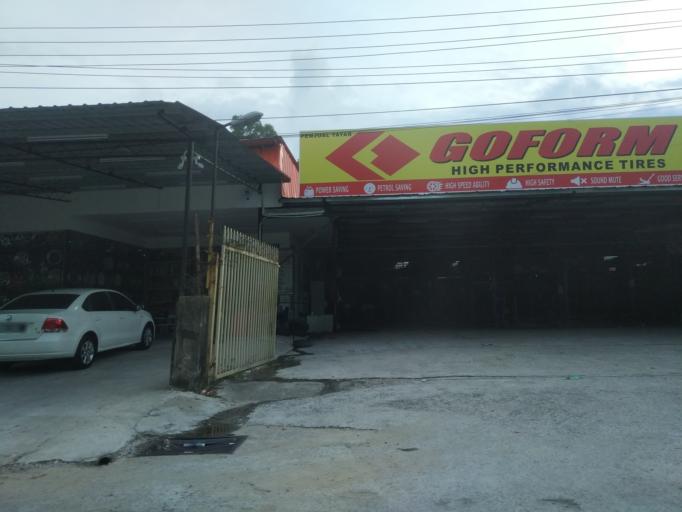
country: MY
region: Sabah
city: Kota Kinabalu
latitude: 5.9922
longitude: 116.1165
